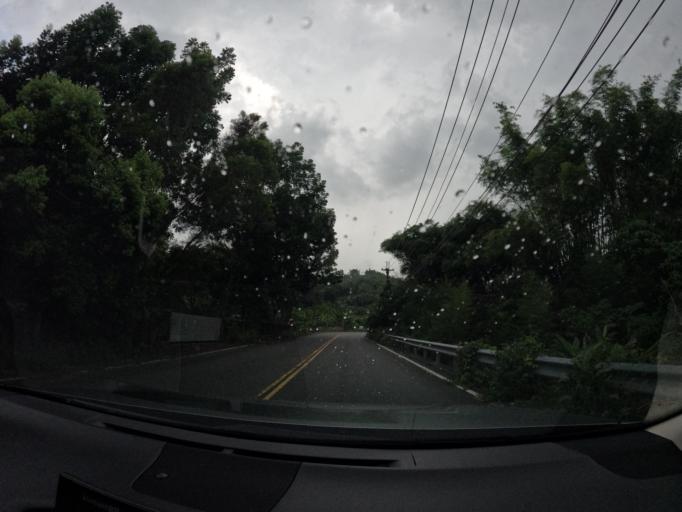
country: TW
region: Taiwan
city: Lugu
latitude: 23.8407
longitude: 120.7722
